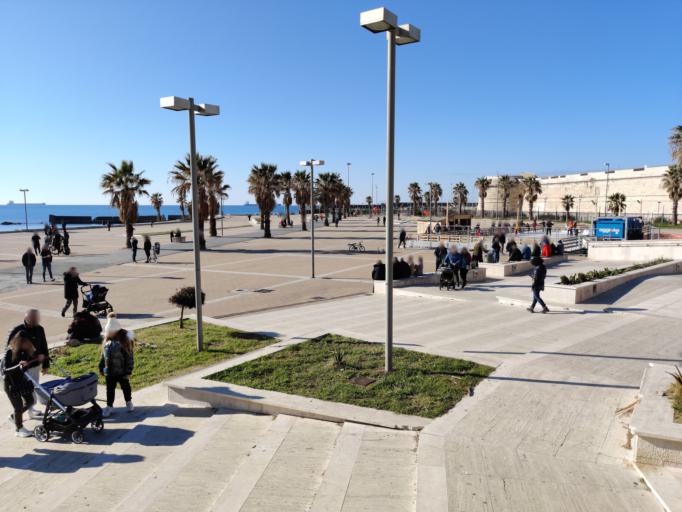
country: IT
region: Latium
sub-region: Citta metropolitana di Roma Capitale
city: Civitavecchia
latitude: 42.0898
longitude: 11.7930
